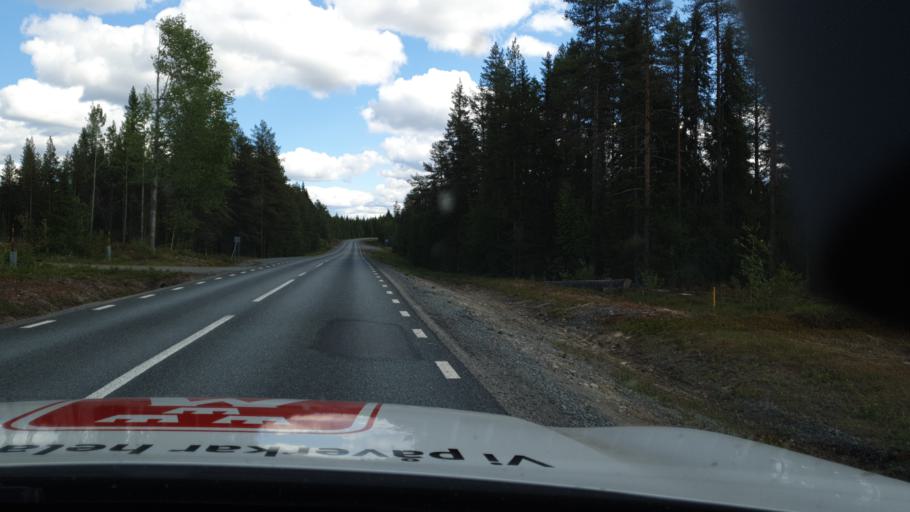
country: SE
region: Vaesterbotten
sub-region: Sorsele Kommun
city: Sorsele
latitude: 65.5587
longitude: 17.8303
